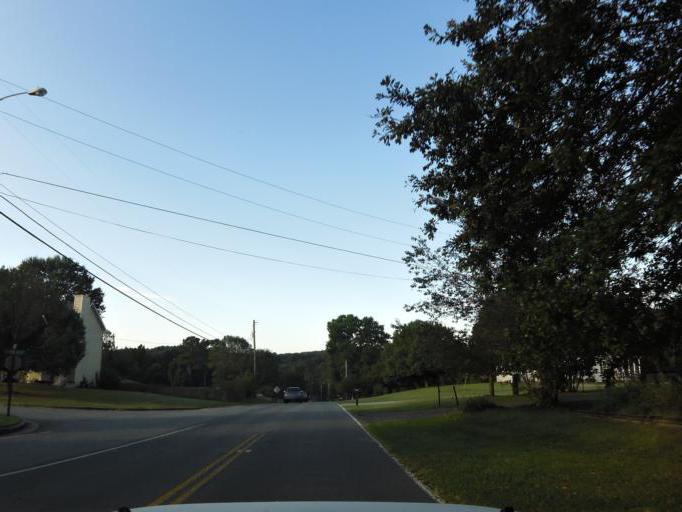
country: US
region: Georgia
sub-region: Cobb County
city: Kennesaw
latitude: 34.0169
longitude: -84.6261
